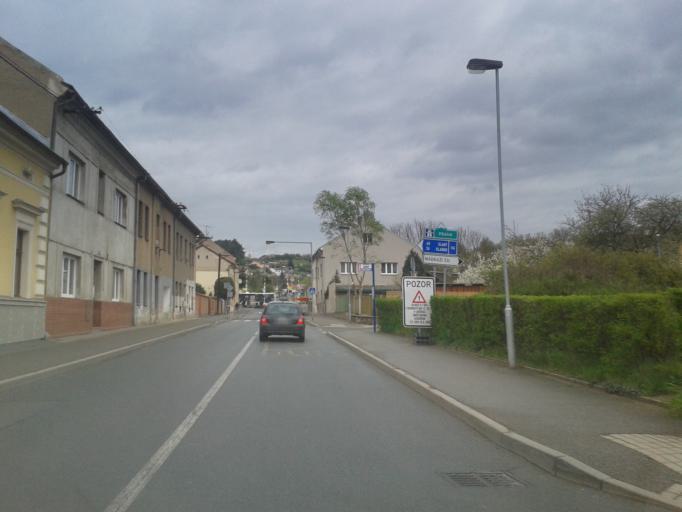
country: CZ
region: Central Bohemia
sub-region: Okres Beroun
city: Beroun
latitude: 49.9671
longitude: 14.0804
